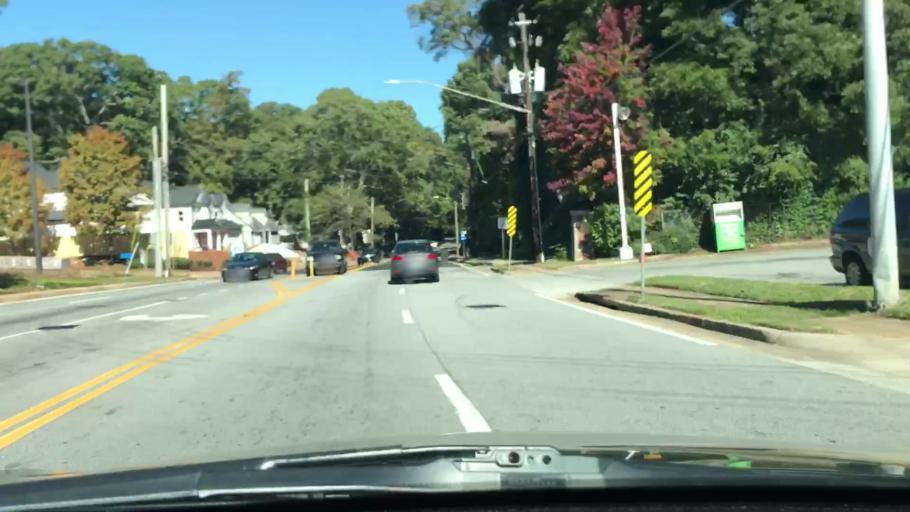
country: US
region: Georgia
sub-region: DeKalb County
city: Belvedere Park
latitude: 33.7473
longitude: -84.2920
